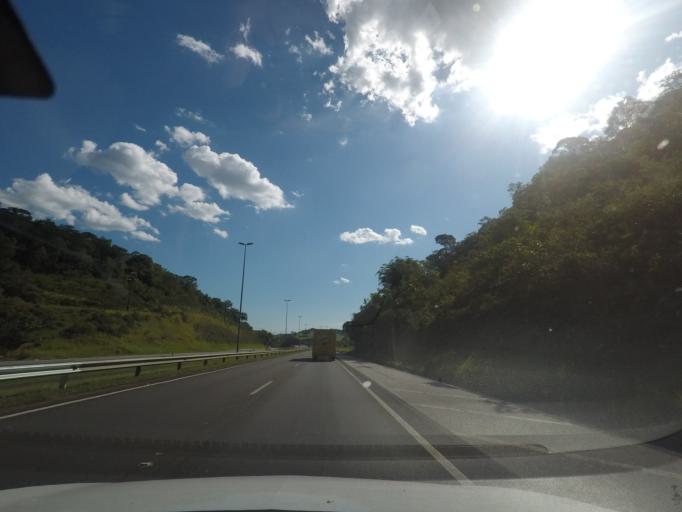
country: BR
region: Rio de Janeiro
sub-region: Guapimirim
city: Guapimirim
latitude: -22.5825
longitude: -43.0140
